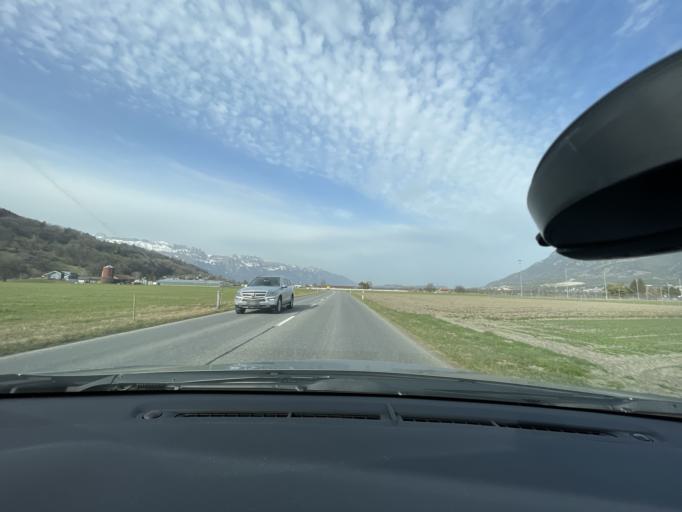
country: CH
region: Saint Gallen
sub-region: Wahlkreis Werdenberg
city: Sevelen
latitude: 47.1315
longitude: 9.4862
